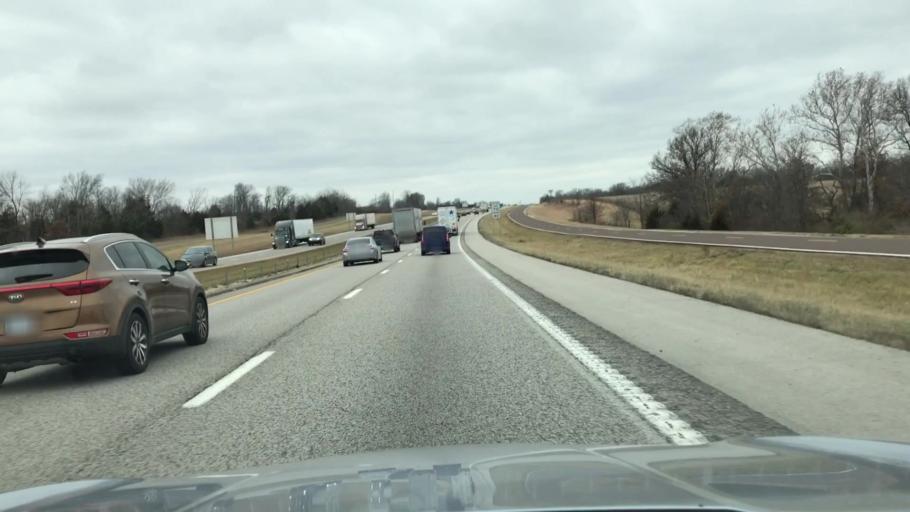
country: US
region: Missouri
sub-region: Warren County
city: Wright City
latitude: 38.8179
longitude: -90.9635
